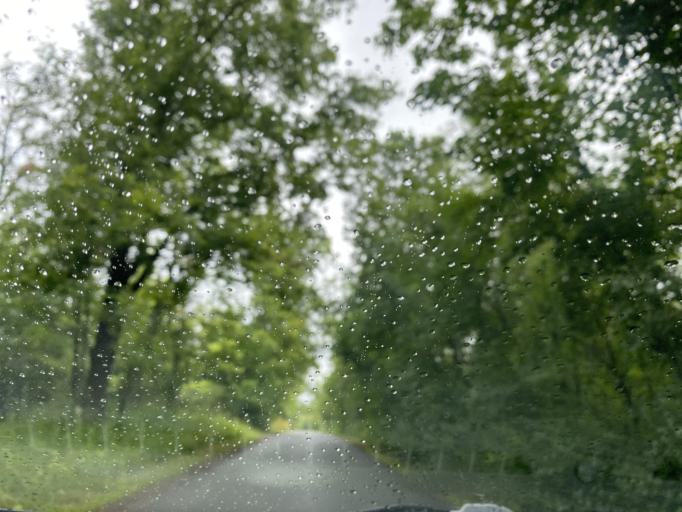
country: CA
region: Quebec
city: Baie-D'Urfe
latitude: 45.4664
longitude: -73.9268
